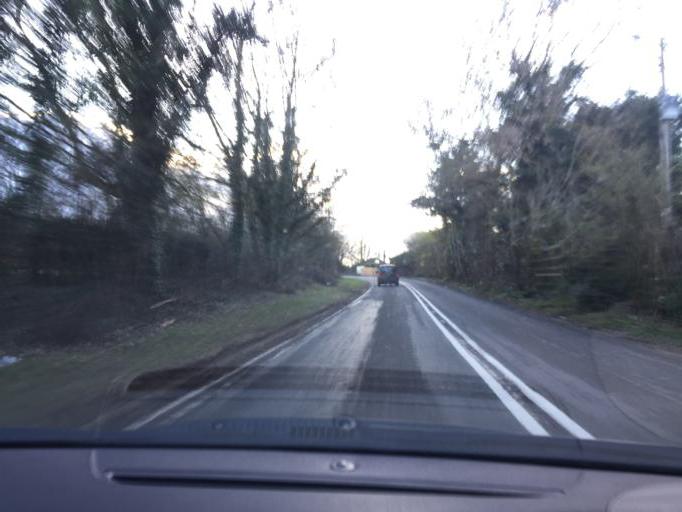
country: GB
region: England
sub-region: Warwickshire
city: Wroxall
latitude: 52.2737
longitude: -1.6671
